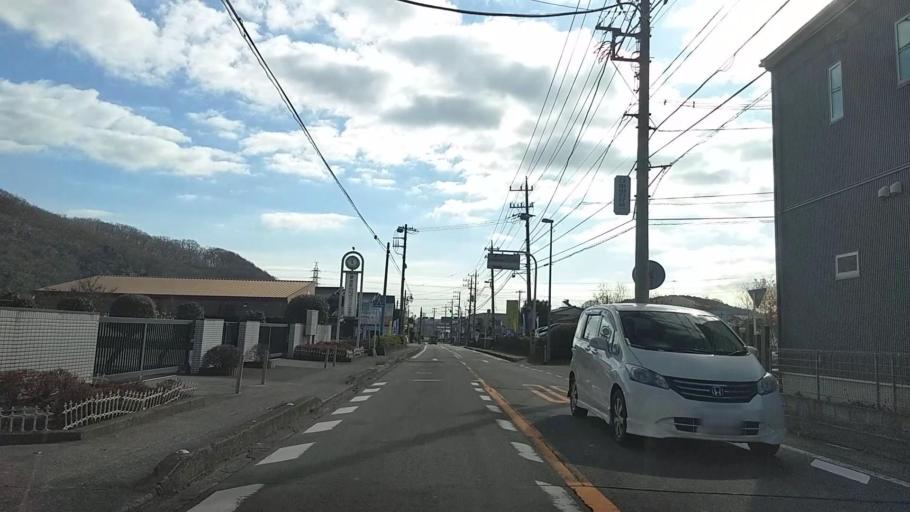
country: JP
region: Kanagawa
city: Isehara
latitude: 35.4435
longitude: 139.2983
